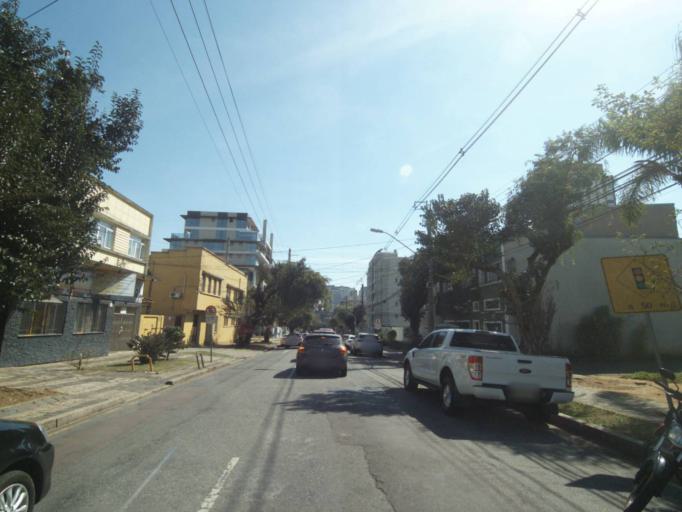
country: BR
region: Parana
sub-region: Curitiba
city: Curitiba
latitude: -25.4523
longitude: -49.2809
